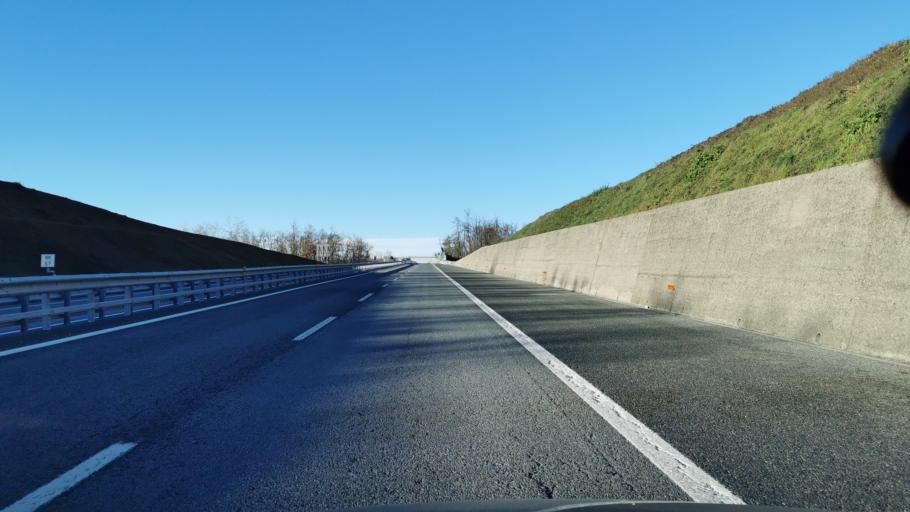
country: IT
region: Piedmont
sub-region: Provincia di Cuneo
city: Magliano Alpi
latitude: 44.4699
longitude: 7.8301
